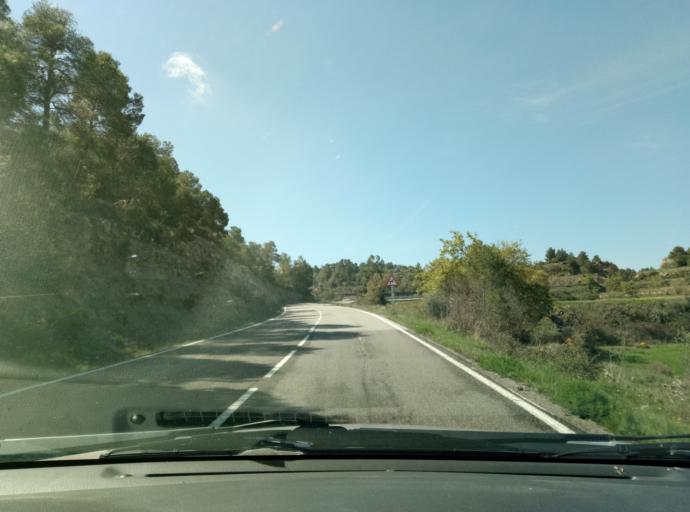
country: ES
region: Catalonia
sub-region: Provincia de Lleida
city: Fulleda
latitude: 41.5125
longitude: 1.0244
